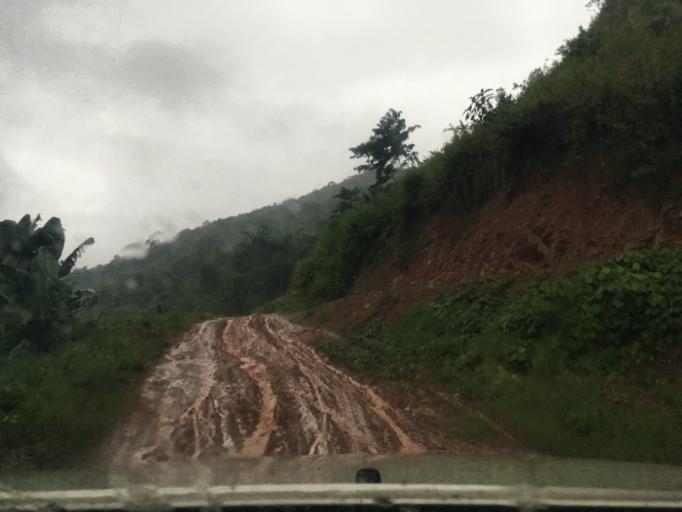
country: LA
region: Oudomxai
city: Muang La
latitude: 21.2412
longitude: 101.9510
